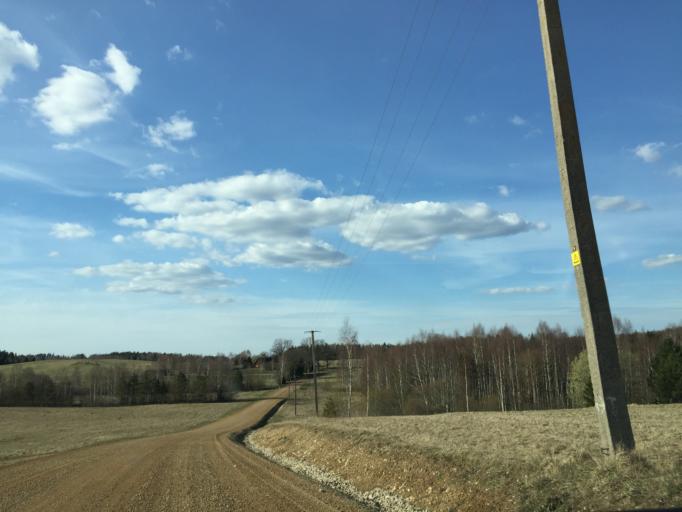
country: EE
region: Tartu
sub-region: Elva linn
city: Elva
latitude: 58.0822
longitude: 26.5199
